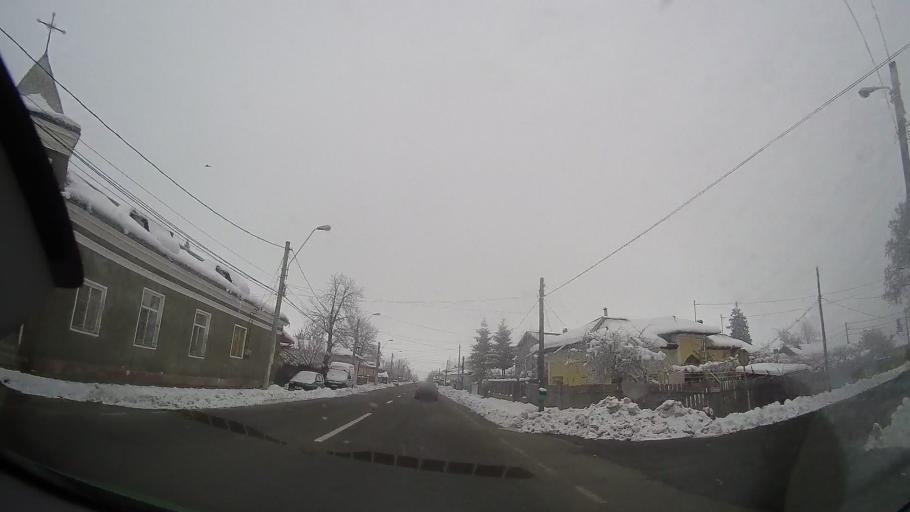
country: RO
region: Neamt
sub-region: Municipiul Roman
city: Roman
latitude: 46.9312
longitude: 26.9392
